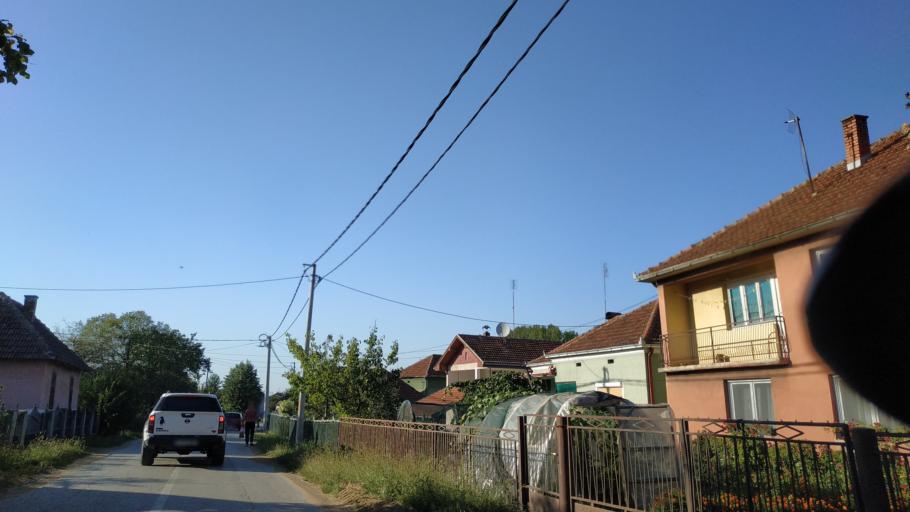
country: RS
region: Central Serbia
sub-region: Rasinski Okrug
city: Krusevac
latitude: 43.4899
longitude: 21.3464
